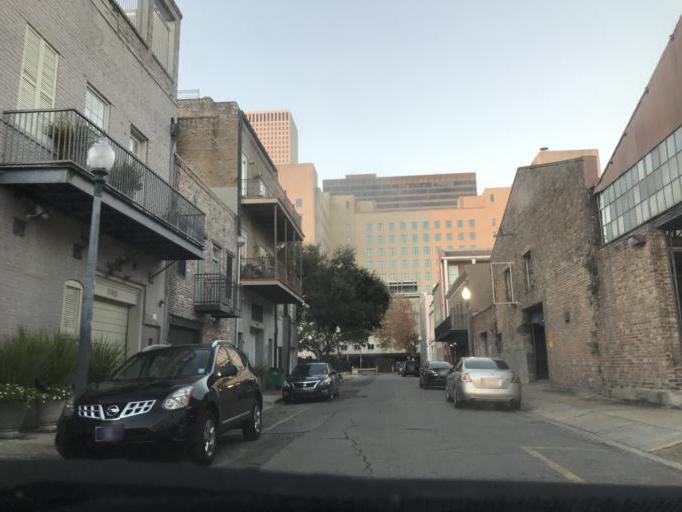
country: US
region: Louisiana
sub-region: Orleans Parish
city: New Orleans
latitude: 29.9462
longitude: -90.0710
